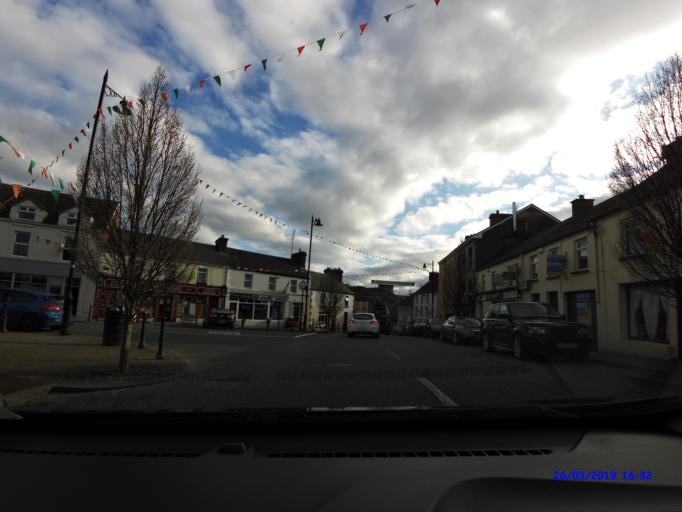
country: IE
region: Connaught
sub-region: Maigh Eo
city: Swinford
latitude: 53.8715
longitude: -8.8502
